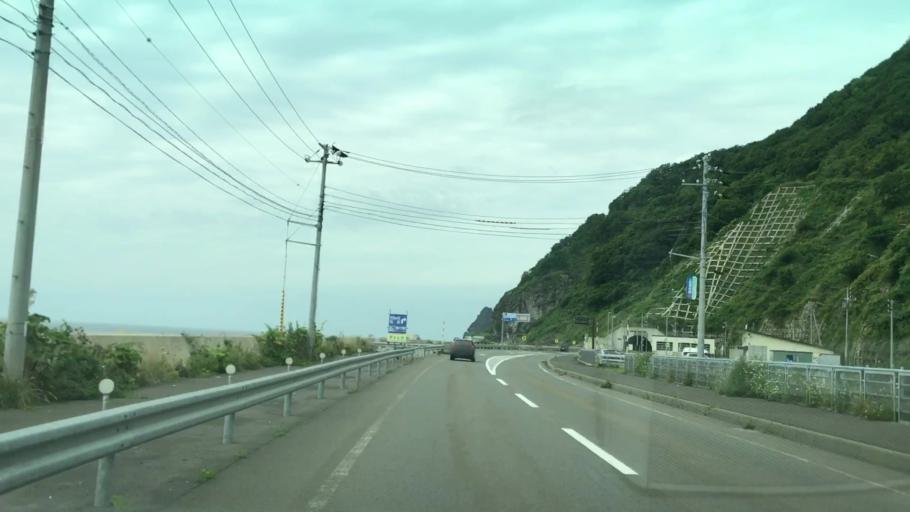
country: JP
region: Hokkaido
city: Iwanai
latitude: 43.1642
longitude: 140.3865
